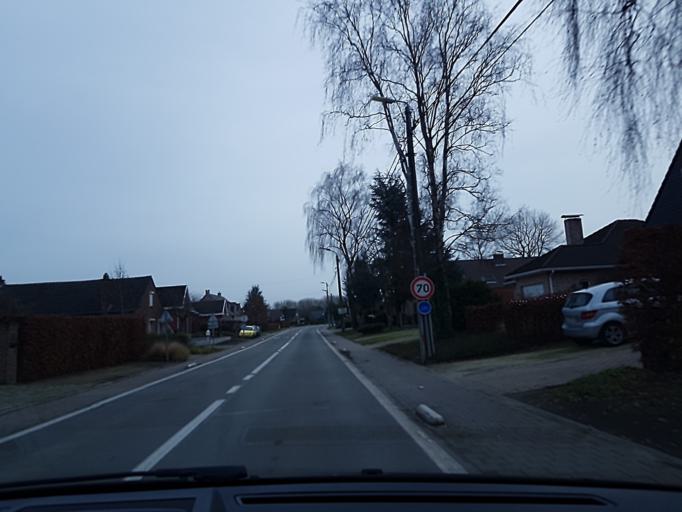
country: BE
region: Flanders
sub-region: Provincie Vlaams-Brabant
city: Keerbergen
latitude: 51.0193
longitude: 4.6476
